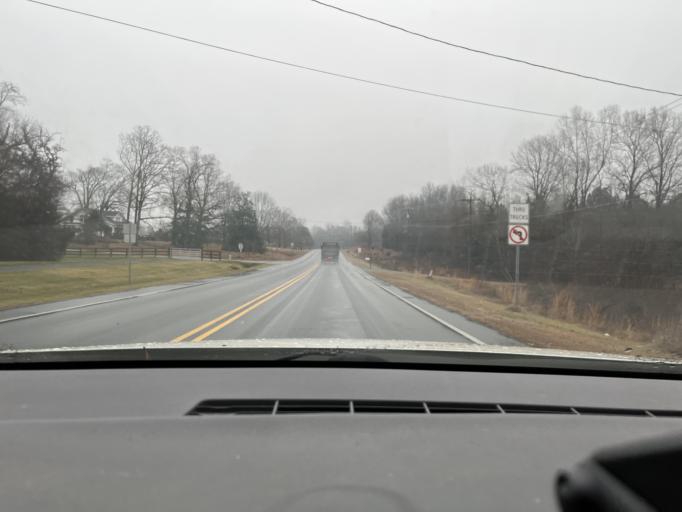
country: US
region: North Carolina
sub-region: Guilford County
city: Pleasant Garden
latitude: 35.9998
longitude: -79.7461
